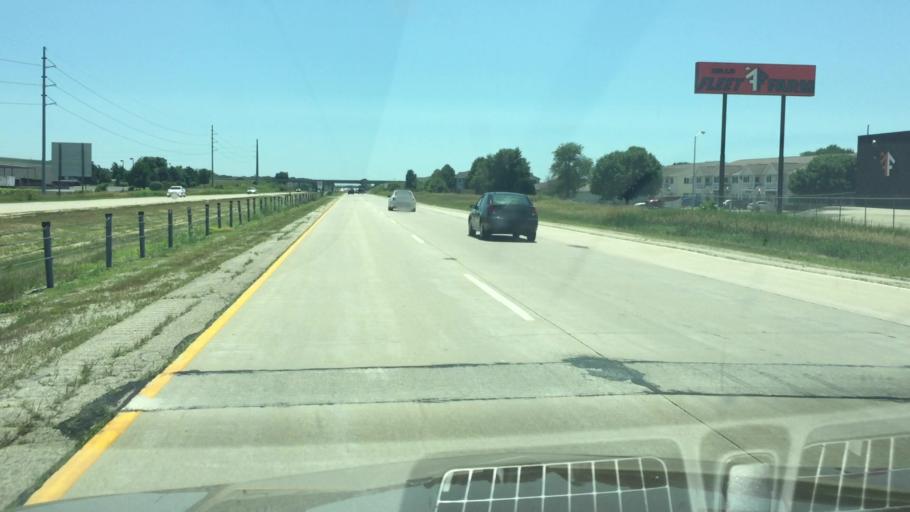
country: US
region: Wisconsin
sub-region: Dodge County
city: Beaver Dam
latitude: 43.4818
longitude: -88.8155
